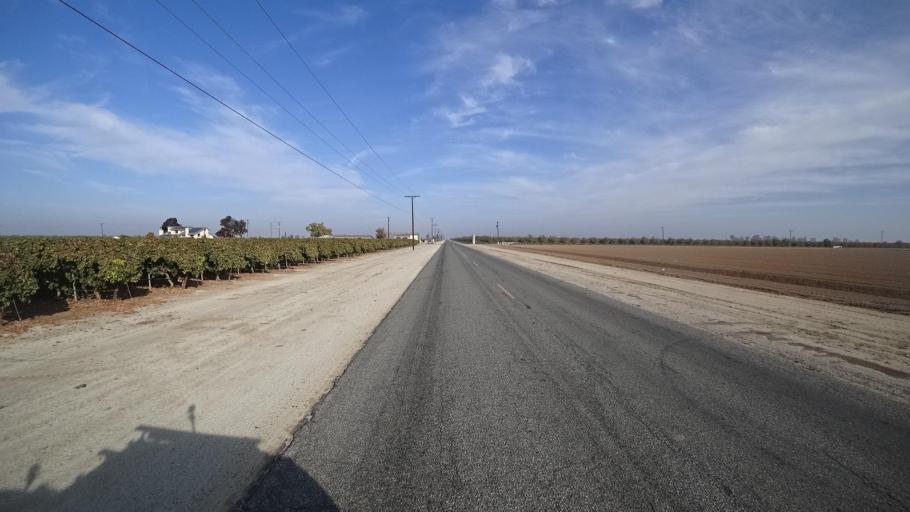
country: US
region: California
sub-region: Kern County
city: McFarland
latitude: 35.6805
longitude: -119.2048
